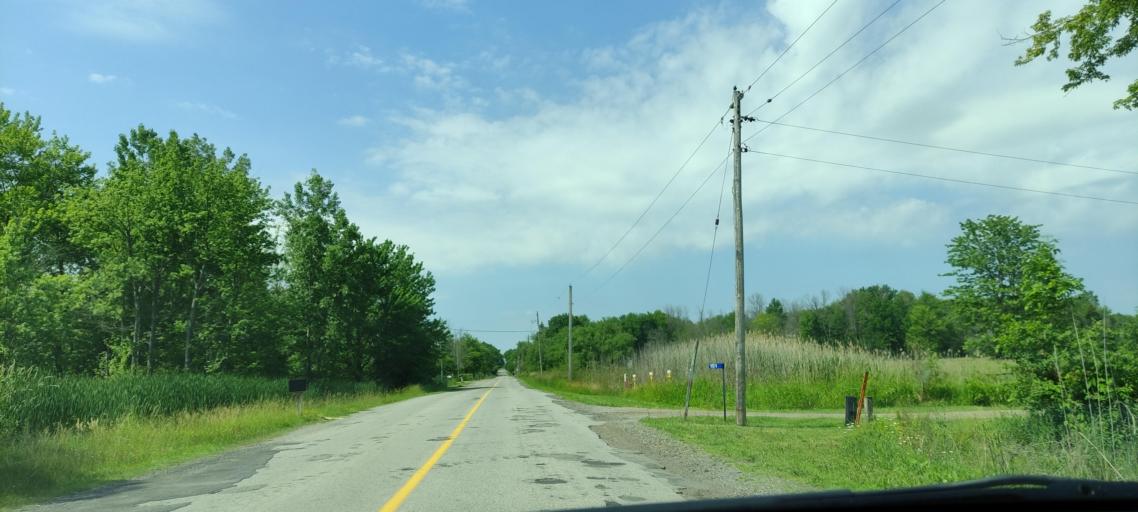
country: CA
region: Ontario
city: Burlington
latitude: 43.3640
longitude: -79.9603
